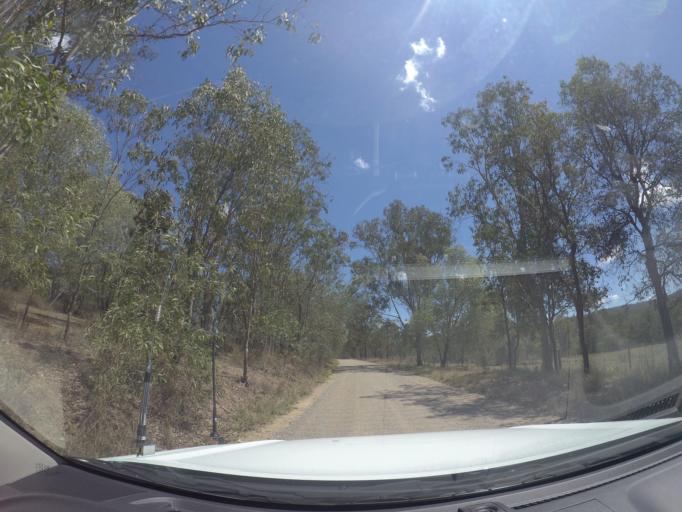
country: AU
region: Queensland
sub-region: Logan
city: North Maclean
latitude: -27.8305
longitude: 152.8659
